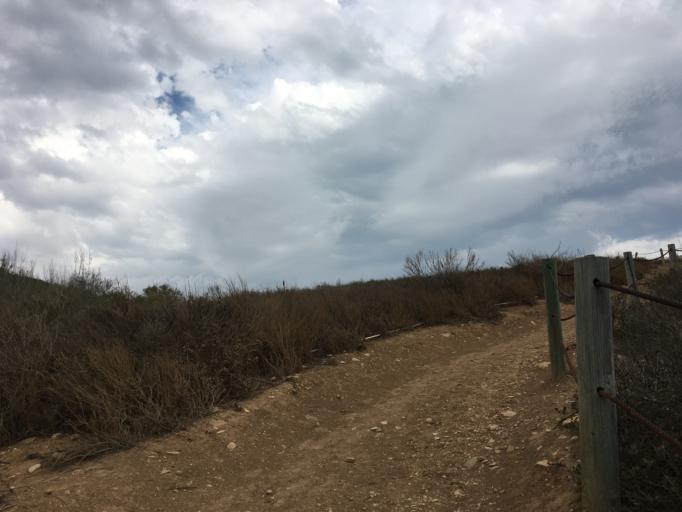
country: US
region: California
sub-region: Los Angeles County
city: Rolling Hills
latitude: 33.7277
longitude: -118.3505
